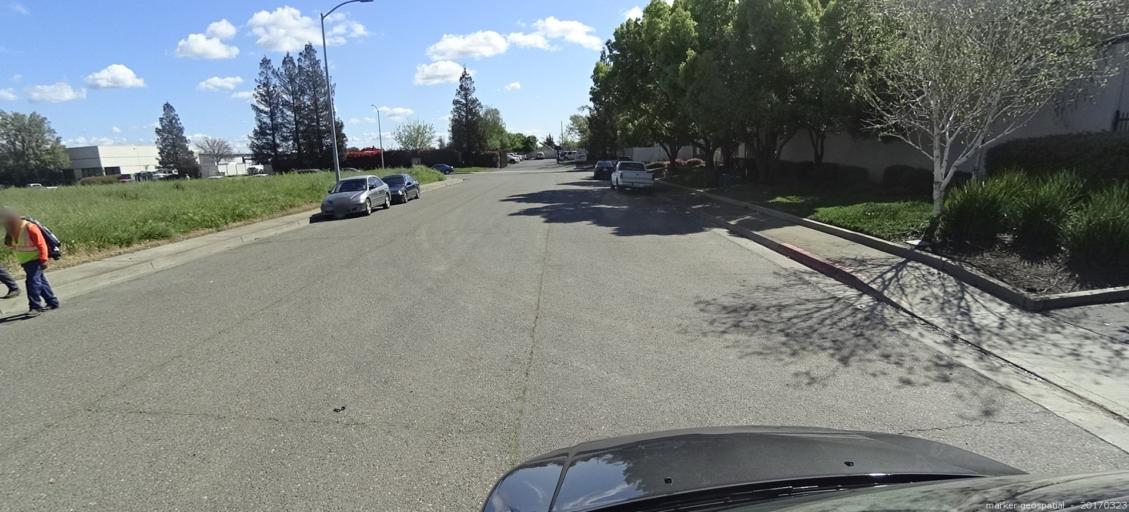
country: US
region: California
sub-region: Sacramento County
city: Florin
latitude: 38.5020
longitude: -121.3942
